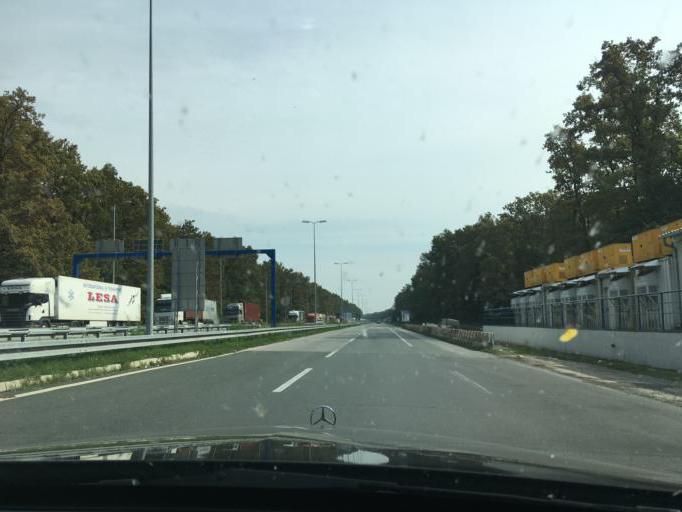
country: HR
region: Vukovarsko-Srijemska
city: Nijemci
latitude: 45.0469
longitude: 19.1105
